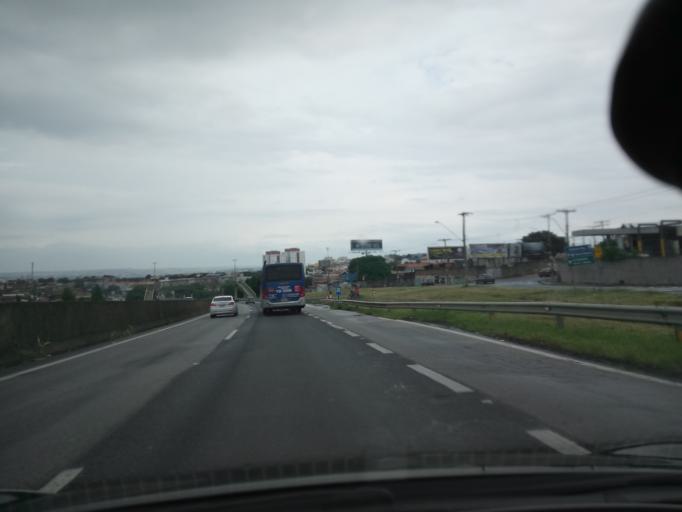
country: BR
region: Sao Paulo
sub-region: Campinas
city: Campinas
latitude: -22.9341
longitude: -47.0800
